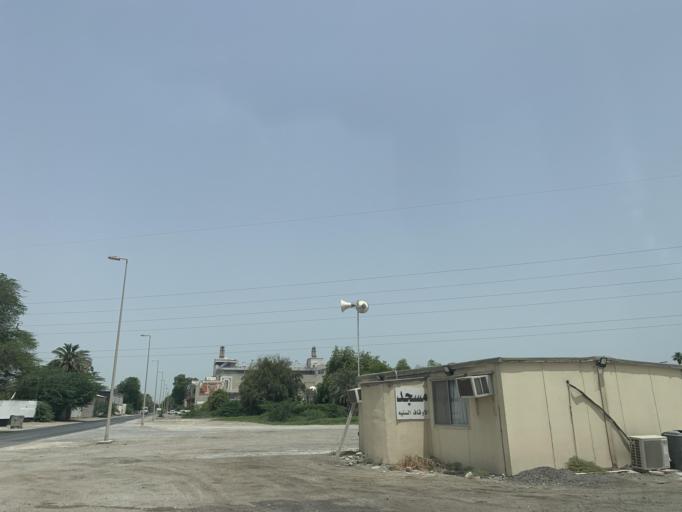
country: BH
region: Northern
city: Ar Rifa'
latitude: 26.1262
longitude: 50.5931
